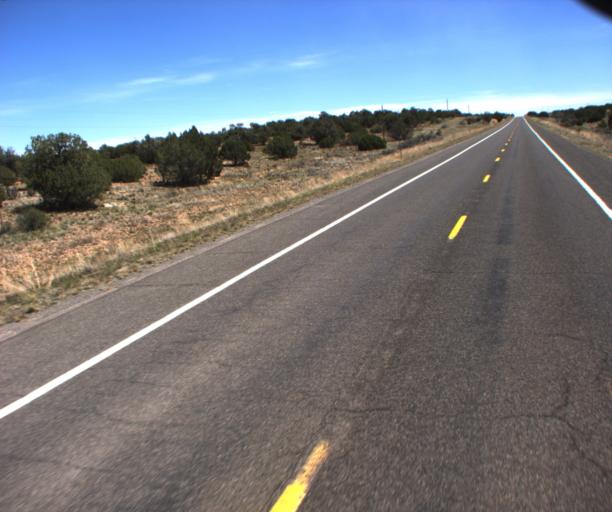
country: US
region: Arizona
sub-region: Mohave County
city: Peach Springs
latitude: 35.5500
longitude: -113.3051
